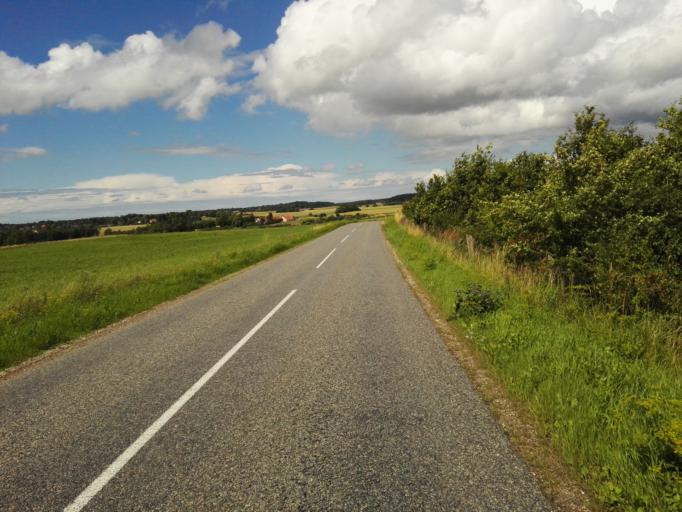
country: DK
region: Capital Region
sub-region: Egedal Kommune
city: Ganlose
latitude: 55.7860
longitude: 12.2341
